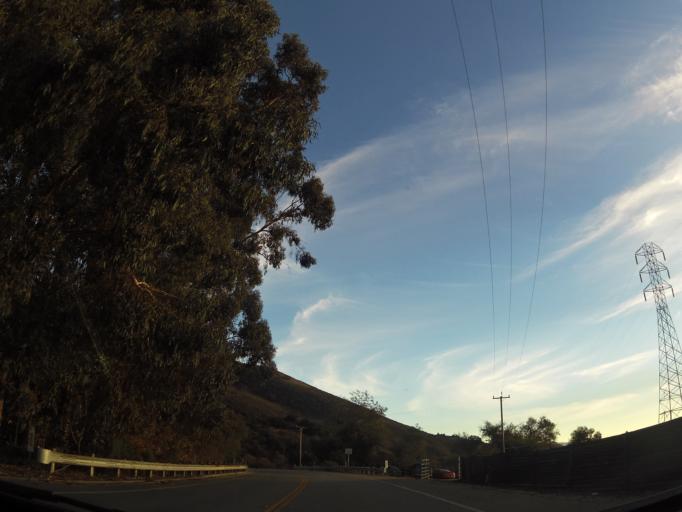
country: US
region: California
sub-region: Monterey County
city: Prunedale
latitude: 36.7720
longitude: -121.6027
